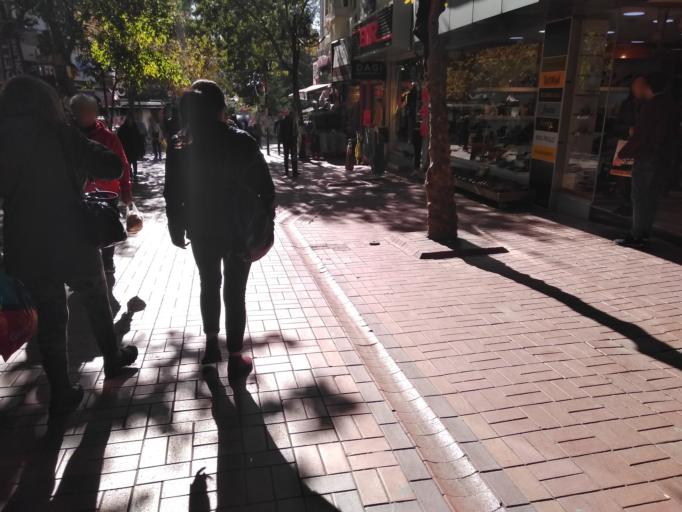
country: TR
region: Istanbul
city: Maltepe
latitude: 40.9238
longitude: 29.1307
